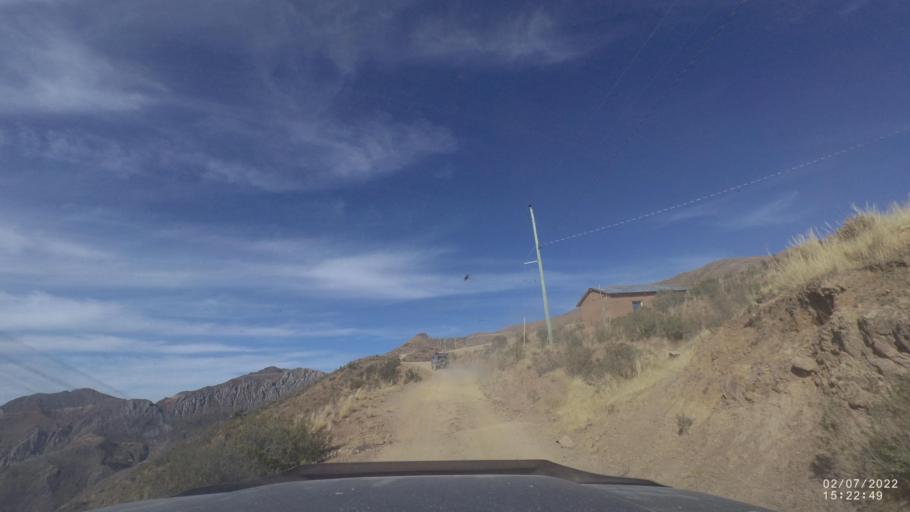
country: BO
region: Cochabamba
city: Irpa Irpa
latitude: -17.8733
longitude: -66.4224
